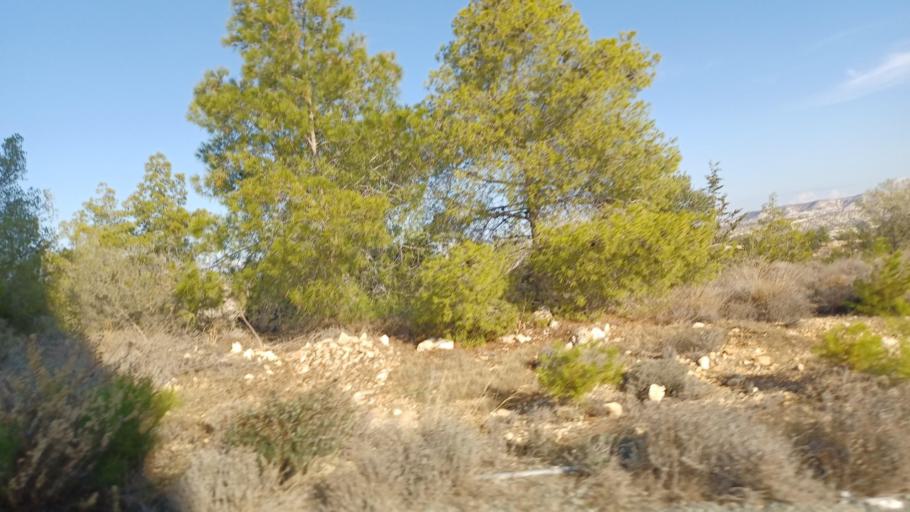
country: CY
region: Larnaka
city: Psevdas
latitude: 34.9582
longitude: 33.5153
